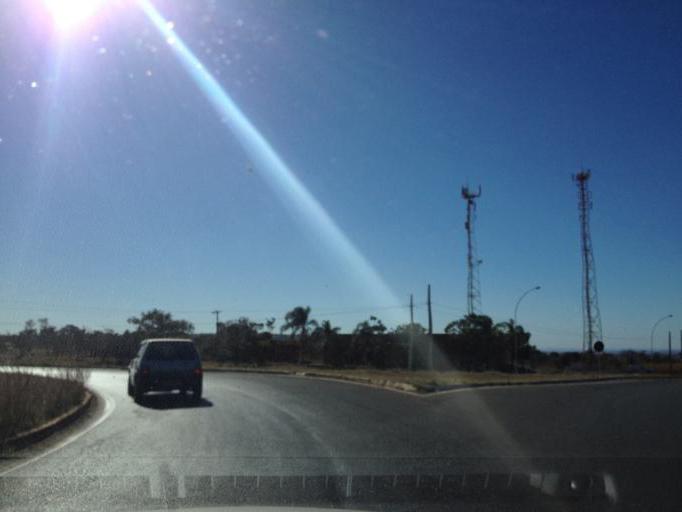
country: BR
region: Federal District
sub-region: Brasilia
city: Brasilia
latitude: -15.6937
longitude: -47.8345
